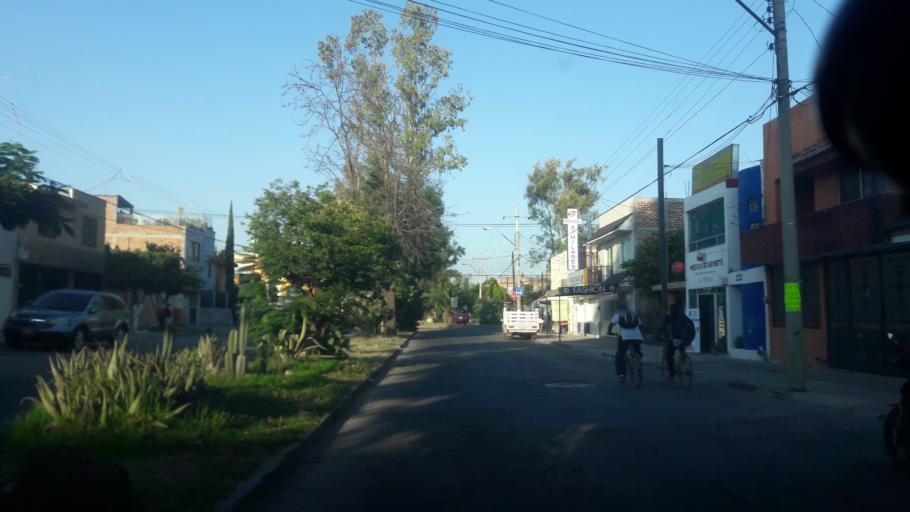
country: MX
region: Guanajuato
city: Leon
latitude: 21.1768
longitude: -101.6663
